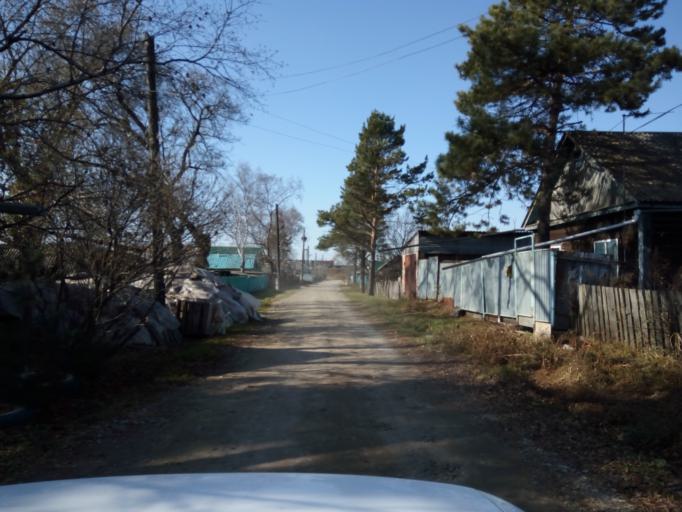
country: RU
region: Primorskiy
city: Dal'nerechensk
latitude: 45.9288
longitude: 133.7152
